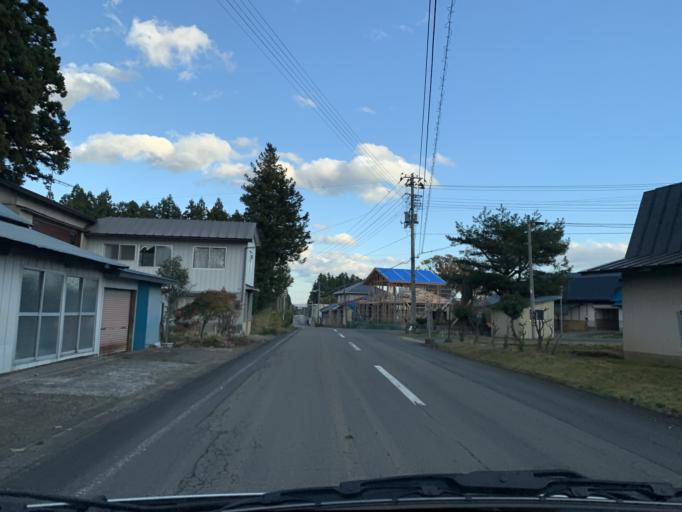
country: JP
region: Iwate
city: Mizusawa
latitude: 39.0770
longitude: 141.0465
